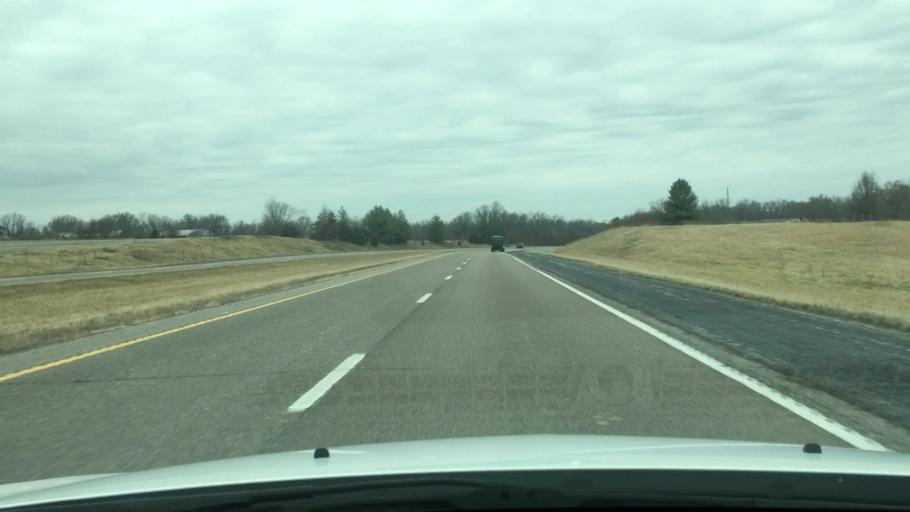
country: US
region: Missouri
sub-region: Audrain County
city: Mexico
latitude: 39.0390
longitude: -91.8917
